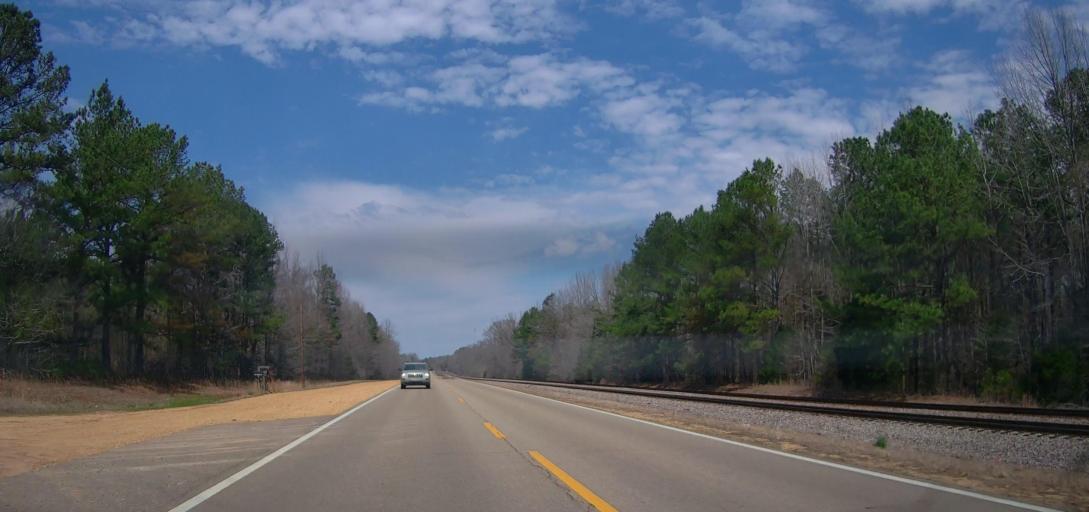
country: US
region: Mississippi
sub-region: Union County
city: New Albany
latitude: 34.5869
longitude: -89.1335
